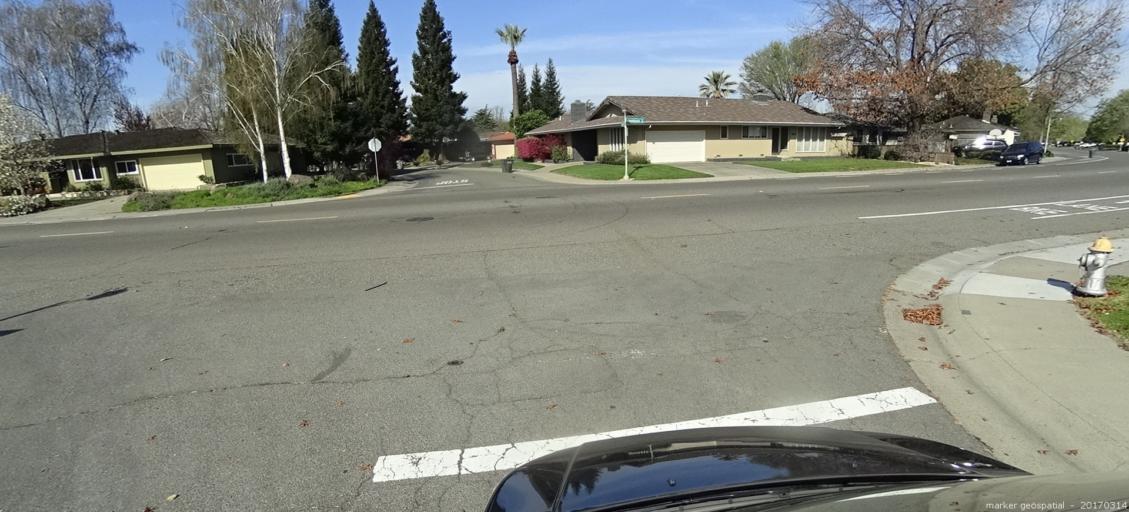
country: US
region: California
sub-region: Sacramento County
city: Parkway
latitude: 38.5094
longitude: -121.5236
